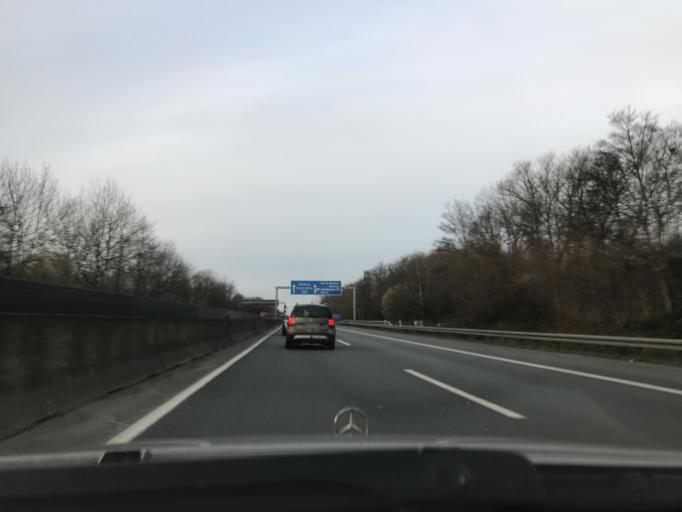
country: DE
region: North Rhine-Westphalia
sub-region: Regierungsbezirk Arnsberg
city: Herne
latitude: 51.5538
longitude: 7.2257
